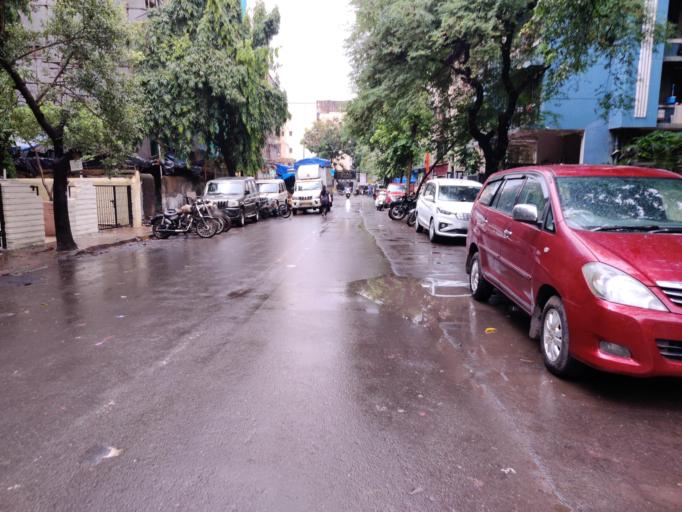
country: IN
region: Maharashtra
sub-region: Mumbai Suburban
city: Borivli
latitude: 19.2561
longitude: 72.8595
